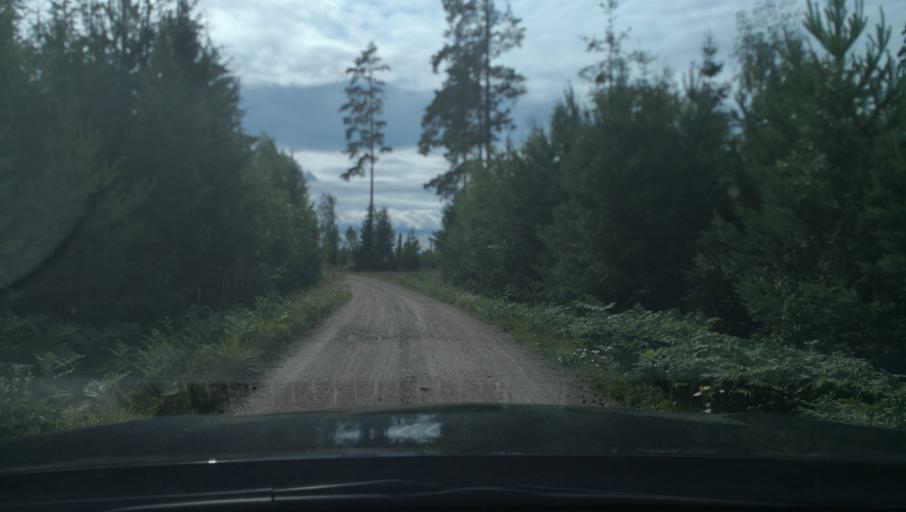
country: SE
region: Vaestmanland
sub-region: Hallstahammars Kommun
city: Hallstahammar
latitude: 59.6487
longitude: 16.0872
